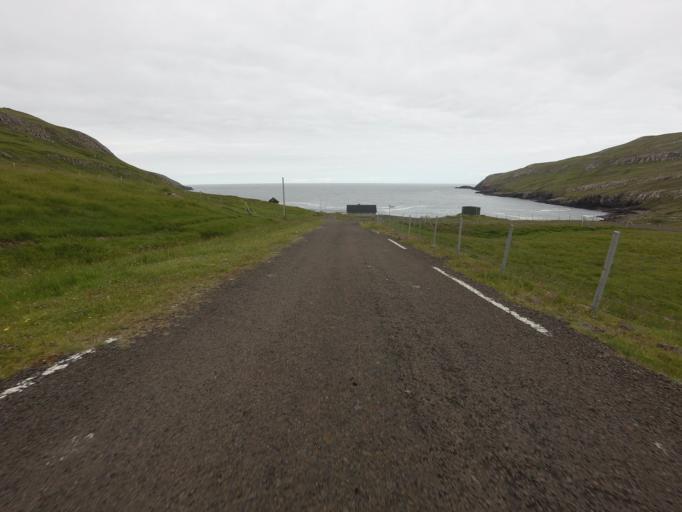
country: FO
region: Suduroy
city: Vagur
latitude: 61.4420
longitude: -6.7262
